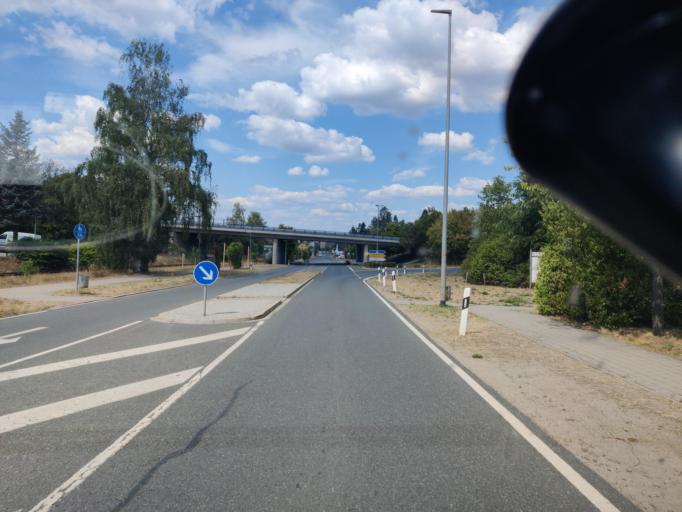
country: DE
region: Bavaria
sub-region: Regierungsbezirk Mittelfranken
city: Roth
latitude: 49.2401
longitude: 11.1063
